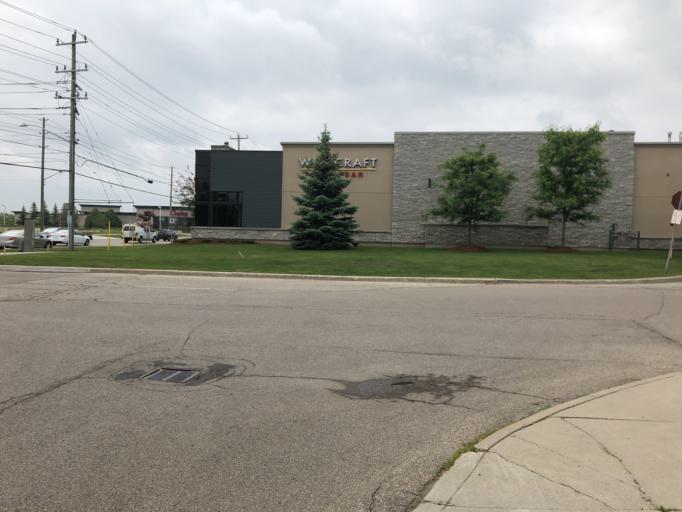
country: CA
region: Ontario
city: Waterloo
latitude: 43.4872
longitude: -80.5278
